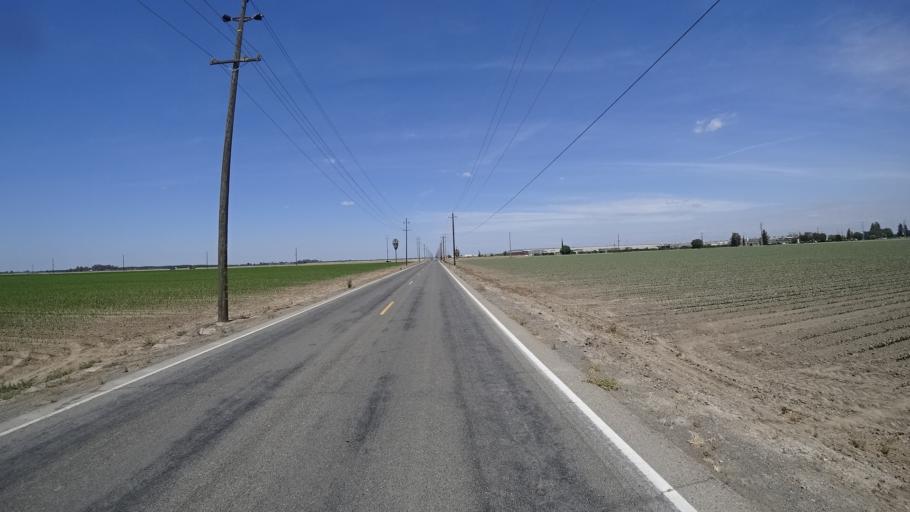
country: US
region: California
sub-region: Kings County
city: Home Garden
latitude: 36.2519
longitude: -119.6549
